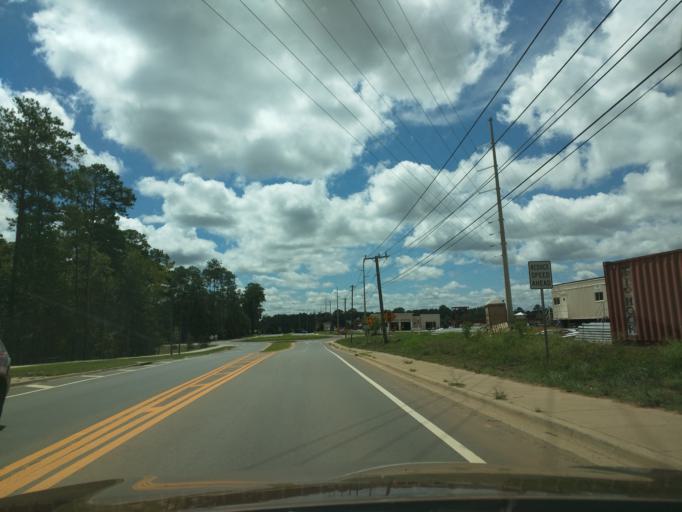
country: US
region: Florida
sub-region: Leon County
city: Tallahassee
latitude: 30.5646
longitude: -84.2208
